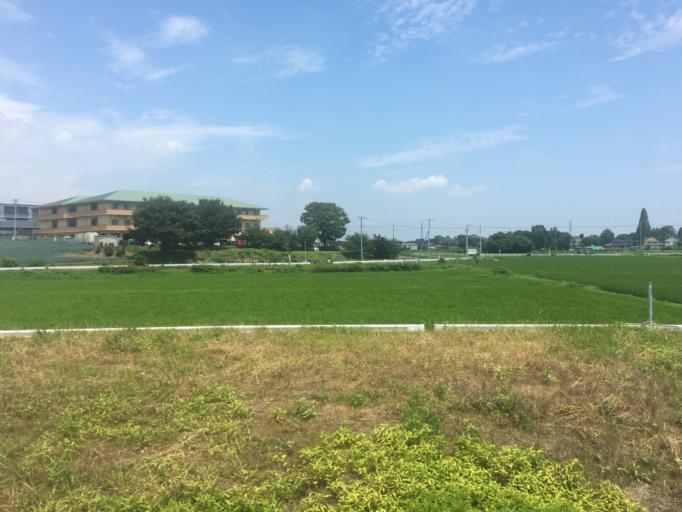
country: JP
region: Saitama
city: Yorii
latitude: 36.1543
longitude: 139.2004
